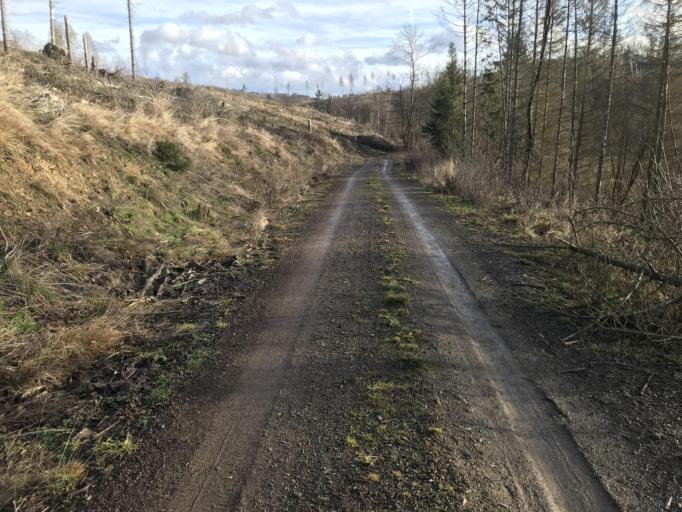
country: DE
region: Saxony-Anhalt
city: Harzgerode
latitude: 51.5739
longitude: 11.1505
